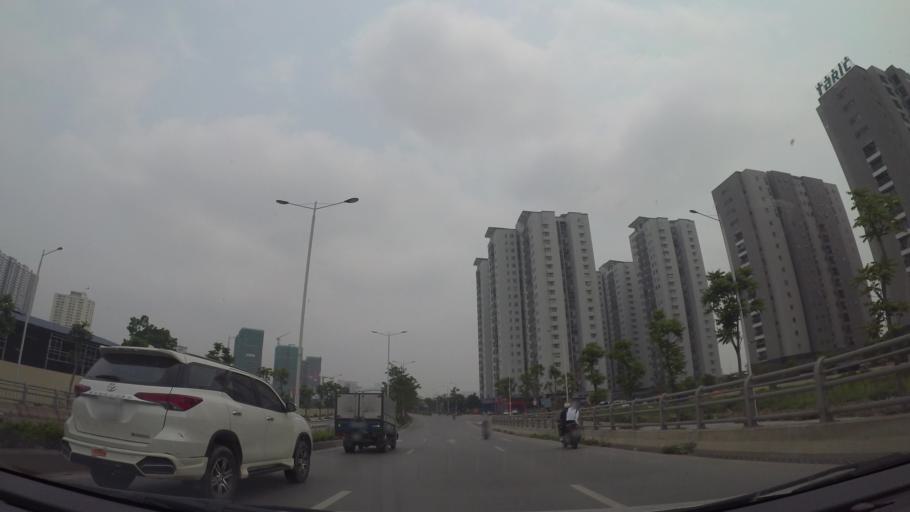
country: VN
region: Ha Noi
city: Cau Dien
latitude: 21.0326
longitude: 105.7545
